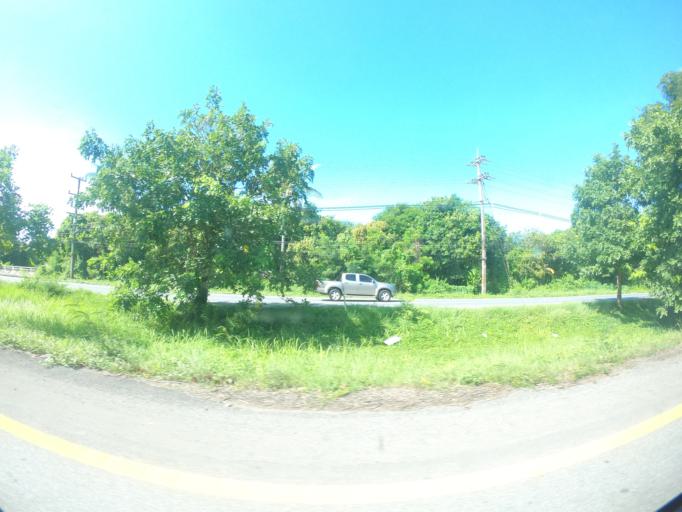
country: TH
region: Nakhon Nayok
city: Nakhon Nayok
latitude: 14.2389
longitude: 101.1468
